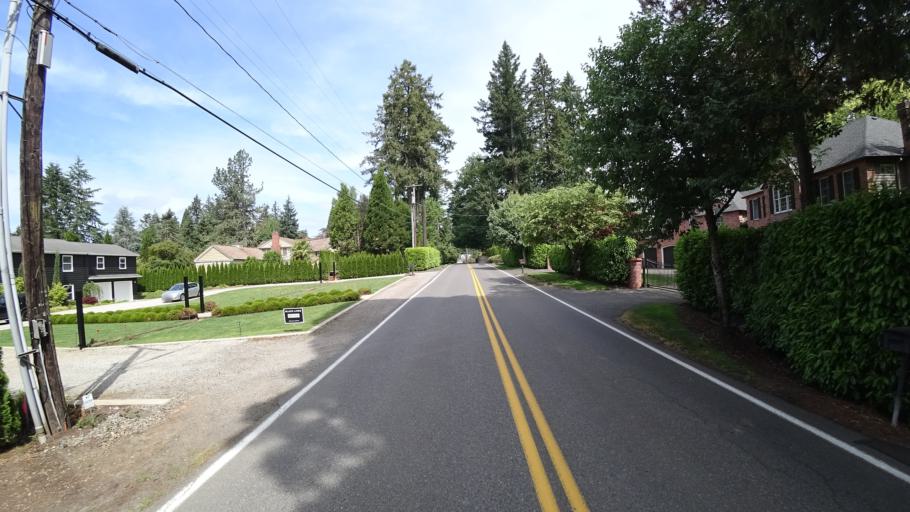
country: US
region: Oregon
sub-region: Clackamas County
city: Lake Oswego
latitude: 45.4428
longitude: -122.6677
